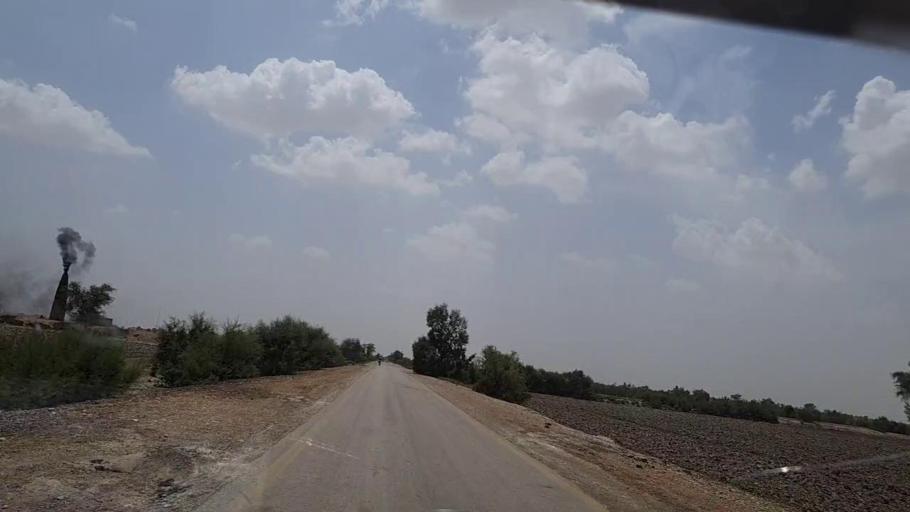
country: PK
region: Sindh
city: Bhan
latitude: 26.5412
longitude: 67.6556
